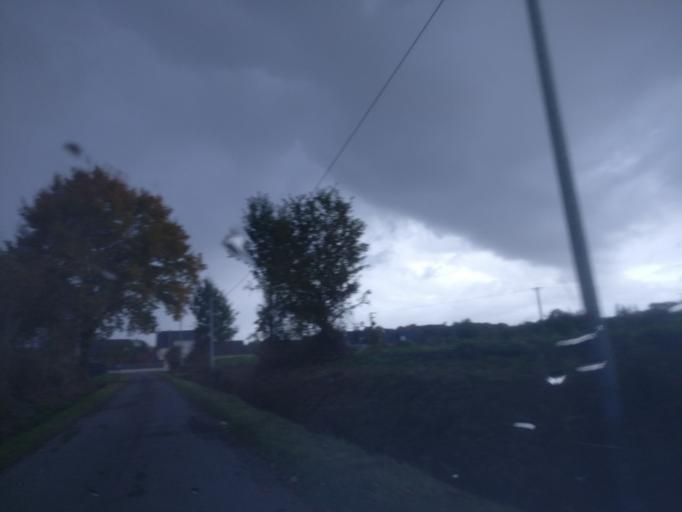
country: FR
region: Brittany
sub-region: Departement d'Ille-et-Vilaine
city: Bruz
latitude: 48.0070
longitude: -1.7808
